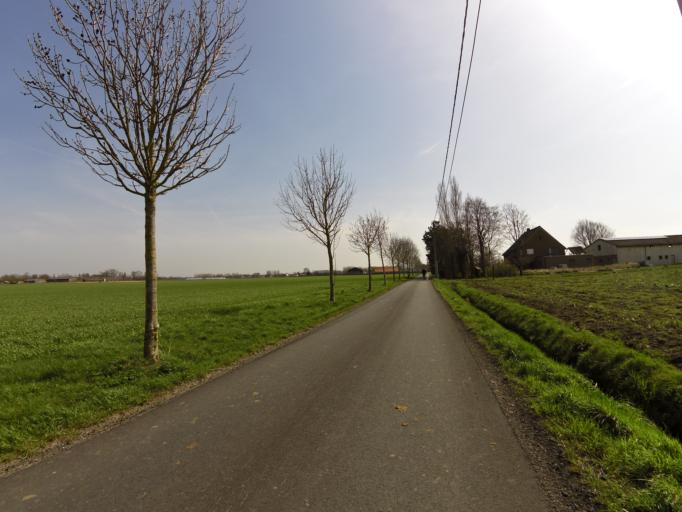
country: BE
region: Flanders
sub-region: Provincie West-Vlaanderen
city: Koekelare
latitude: 51.1064
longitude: 2.9477
